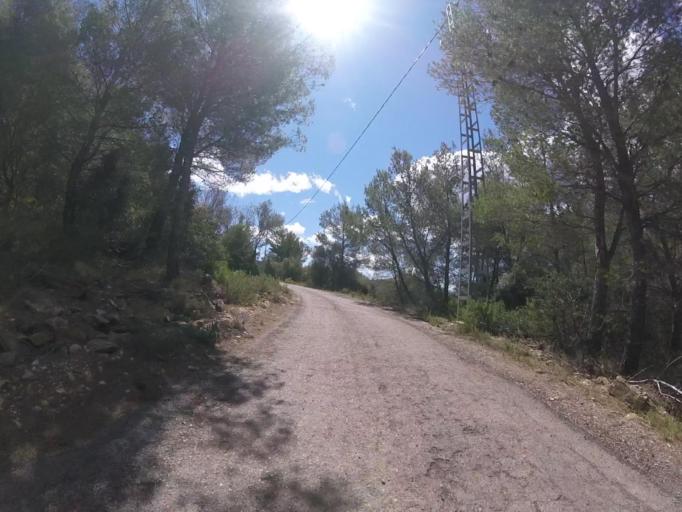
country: ES
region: Valencia
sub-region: Provincia de Castello
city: Sierra-Engarceran
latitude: 40.2705
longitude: -0.0956
